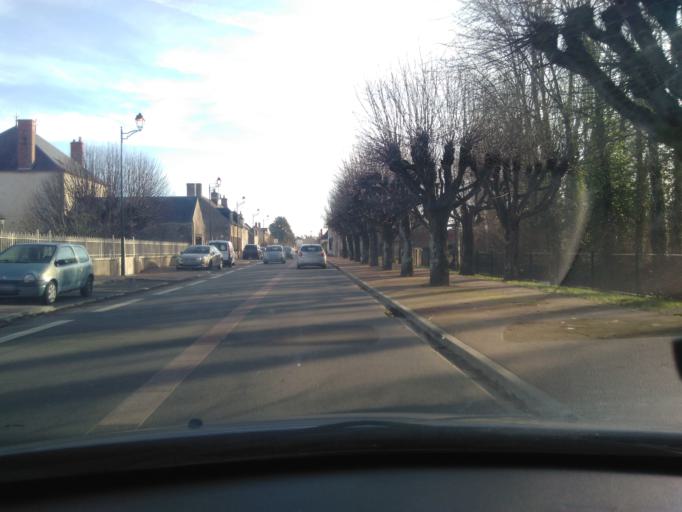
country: FR
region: Centre
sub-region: Departement du Cher
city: Saint-Amand-Montrond
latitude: 46.7228
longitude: 2.5123
